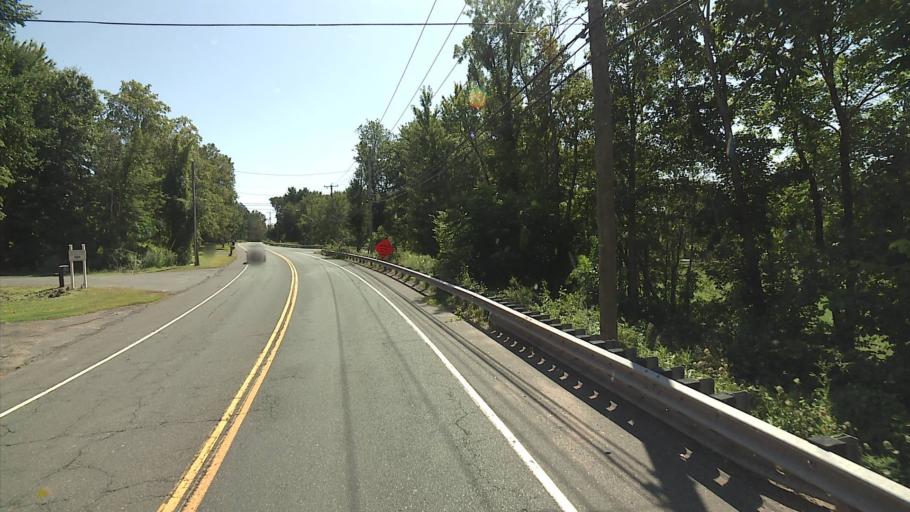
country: US
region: Connecticut
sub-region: Hartford County
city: Windsor Locks
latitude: 41.9571
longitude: -72.6280
